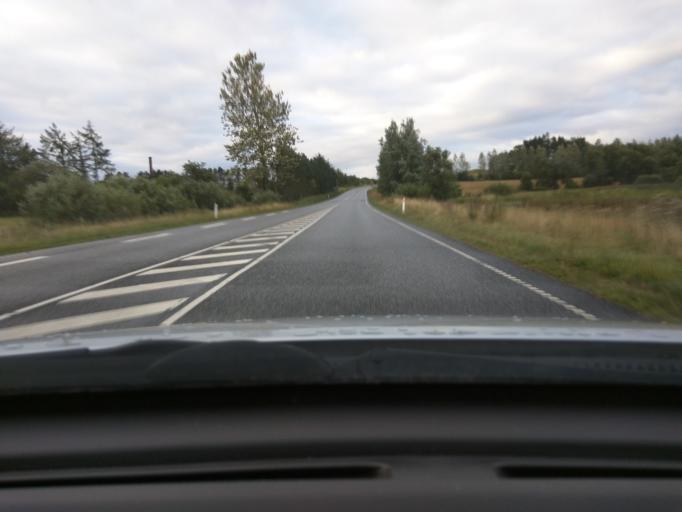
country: DK
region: Central Jutland
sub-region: Silkeborg Kommune
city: Kjellerup
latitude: 56.3254
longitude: 9.3331
